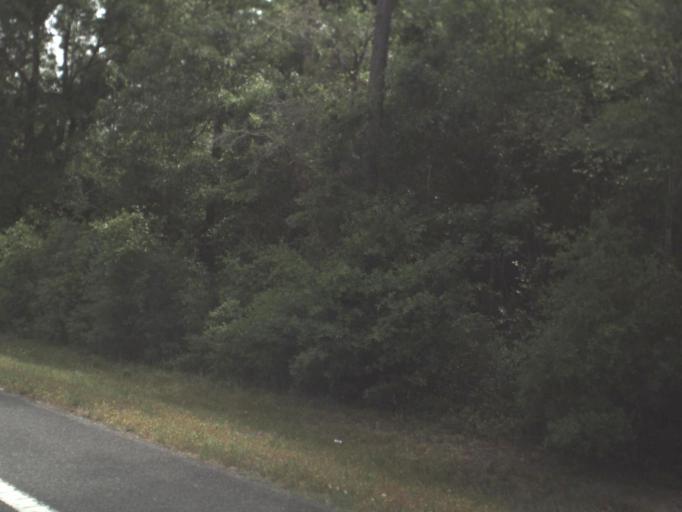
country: US
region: Florida
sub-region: Santa Rosa County
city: Point Baker
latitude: 30.7354
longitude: -87.0930
